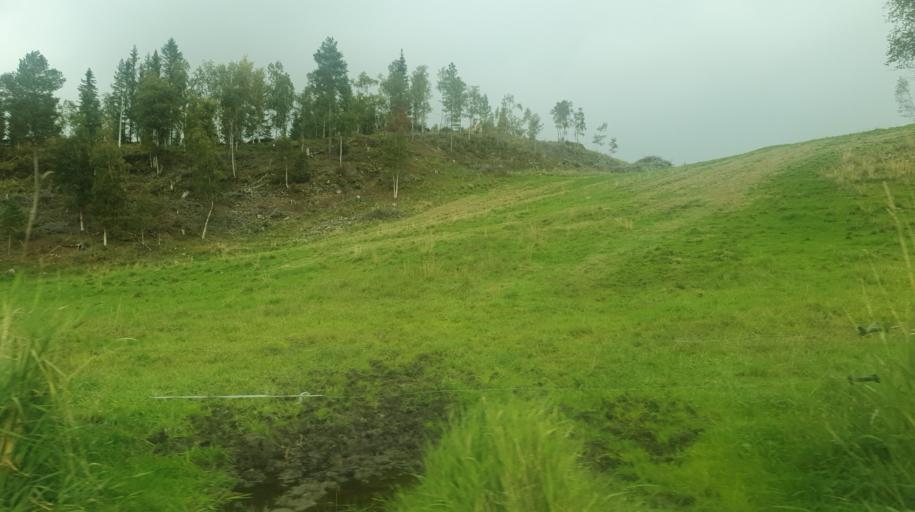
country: NO
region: Nord-Trondelag
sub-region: Levanger
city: Skogn
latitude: 63.6181
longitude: 11.1982
